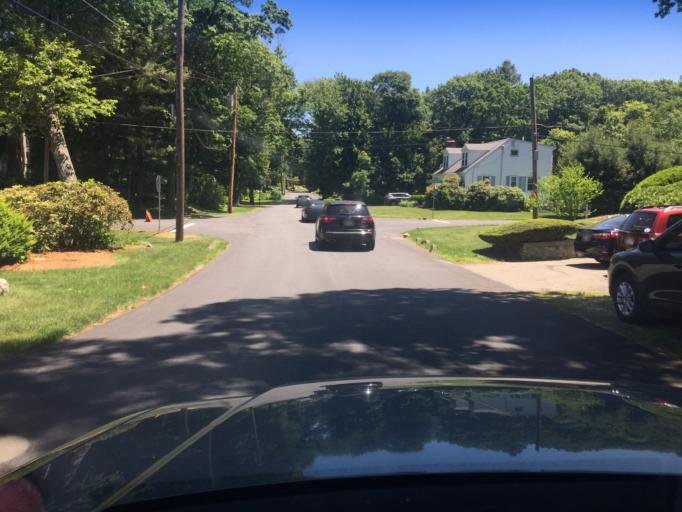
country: US
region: Massachusetts
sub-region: Norfolk County
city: Westwood
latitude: 42.2177
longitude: -71.2317
